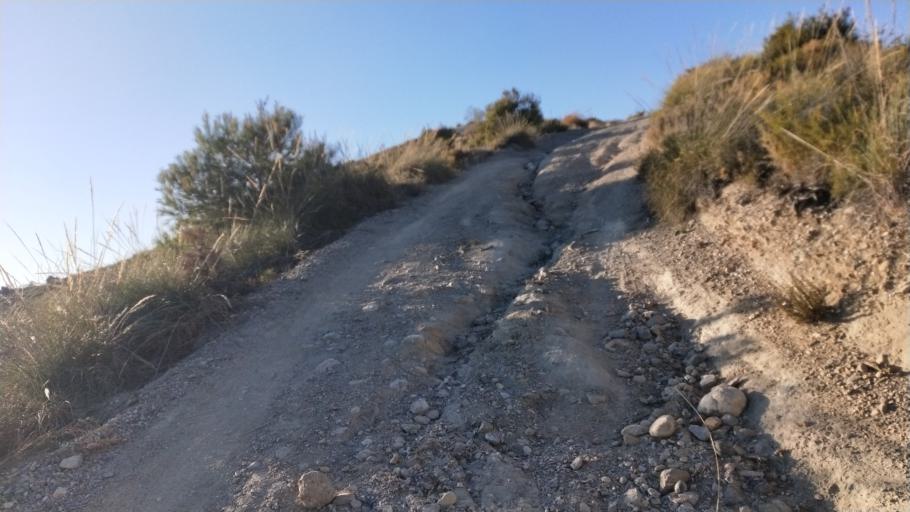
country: ES
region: Andalusia
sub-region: Provincia de Granada
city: Dudar
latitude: 37.1924
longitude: -3.4970
